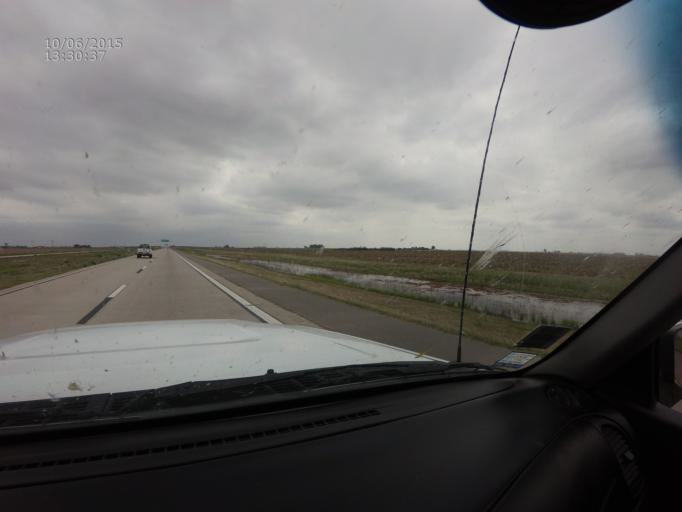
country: AR
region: Cordoba
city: Leones
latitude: -32.6340
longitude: -62.2682
